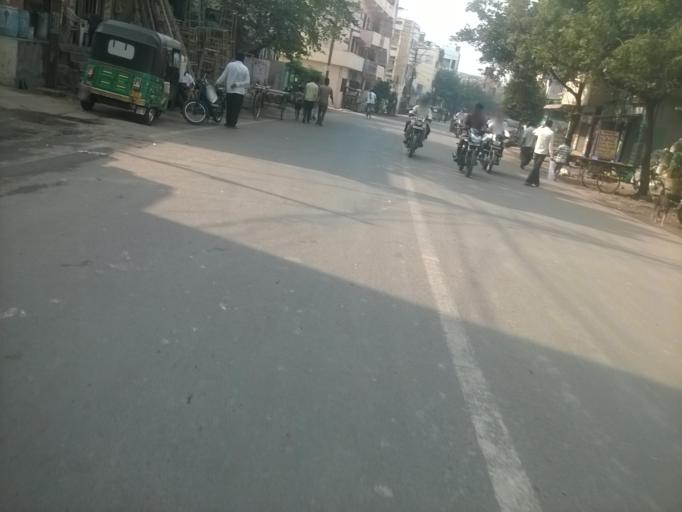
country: IN
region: Andhra Pradesh
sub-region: Krishna
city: Vijayawada
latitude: 16.5238
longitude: 80.6042
